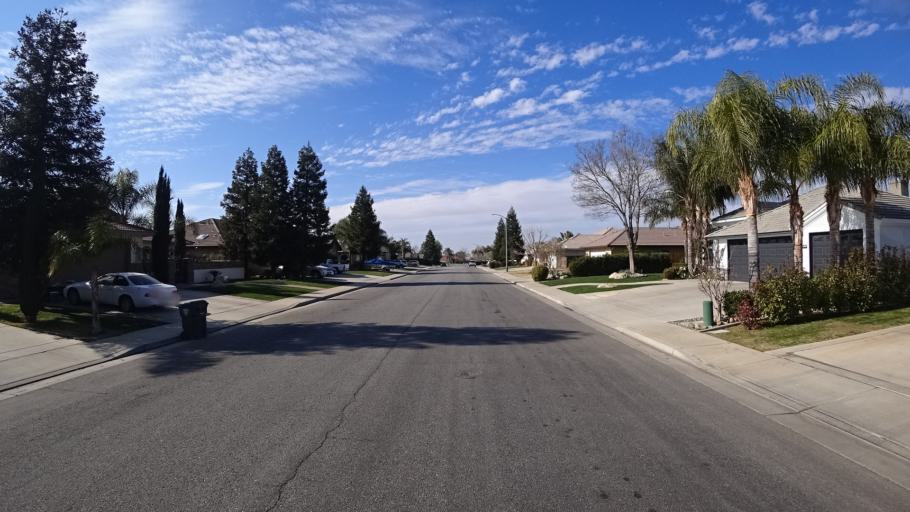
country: US
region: California
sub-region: Kern County
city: Lamont
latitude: 35.3876
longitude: -118.8795
